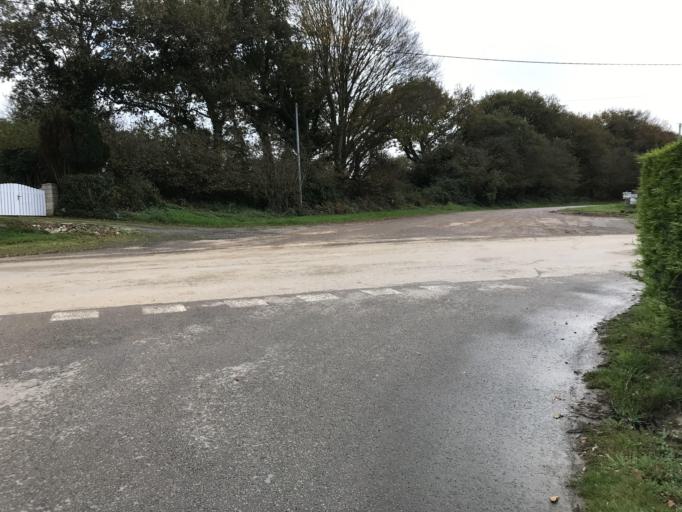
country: FR
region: Brittany
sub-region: Departement du Finistere
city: Irvillac
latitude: 48.3582
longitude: -4.2104
